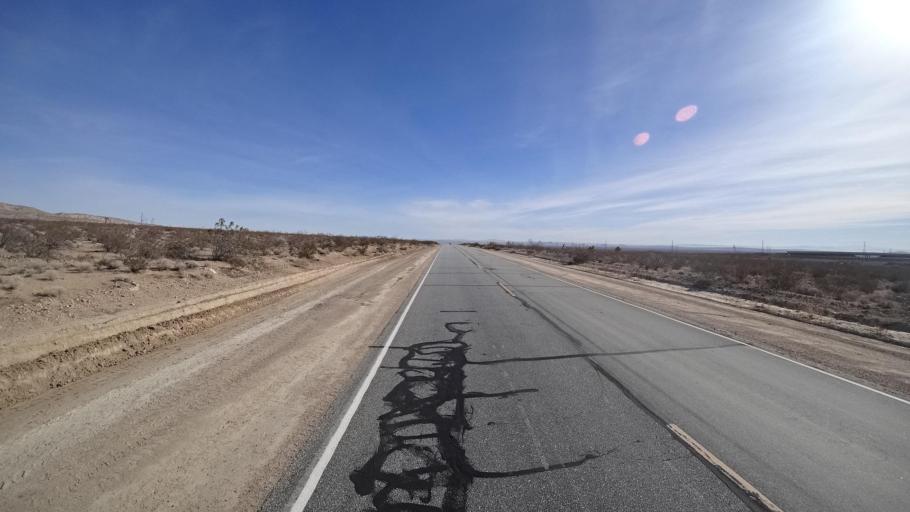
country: US
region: California
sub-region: Kern County
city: Mojave
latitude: 35.1209
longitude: -118.1882
